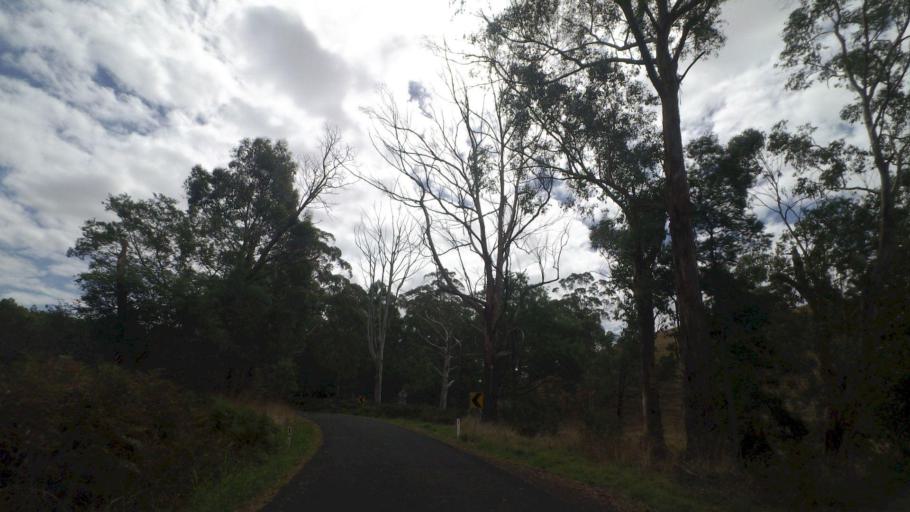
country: AU
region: Victoria
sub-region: Baw Baw
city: Warragul
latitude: -38.3681
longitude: 145.7698
